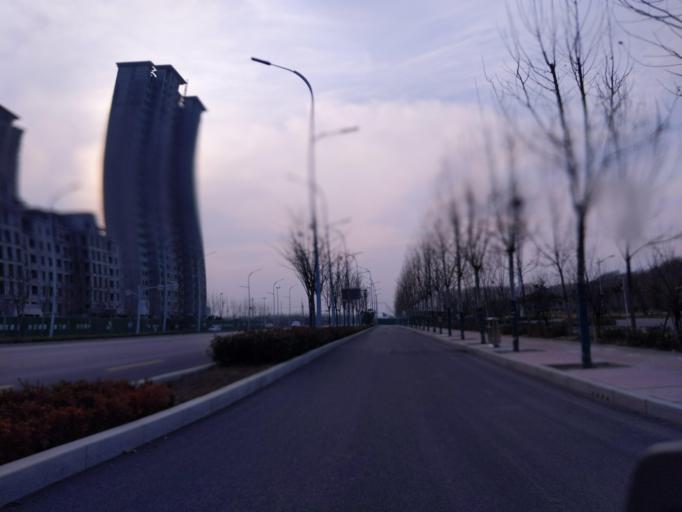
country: CN
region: Henan Sheng
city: Puyang
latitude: 35.8181
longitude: 115.0104
